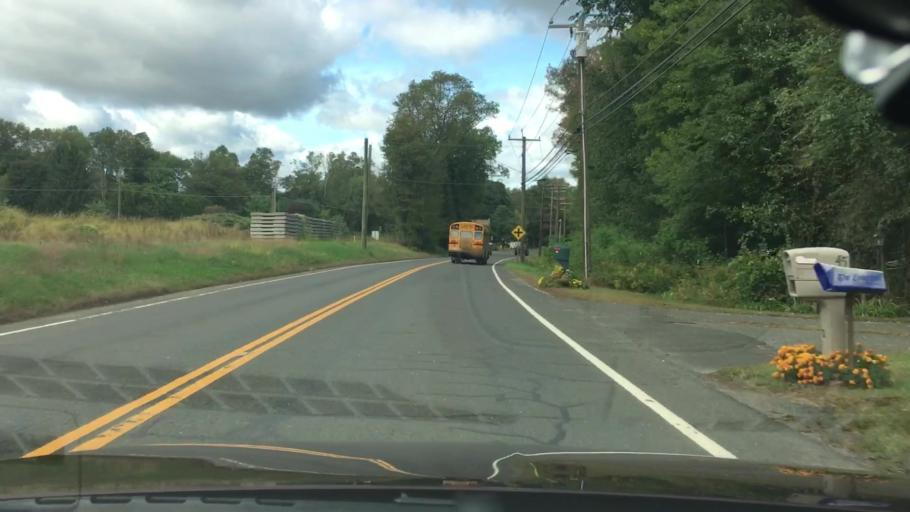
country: US
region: Connecticut
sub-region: Hartford County
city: Hazardville
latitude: 41.9778
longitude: -72.5163
